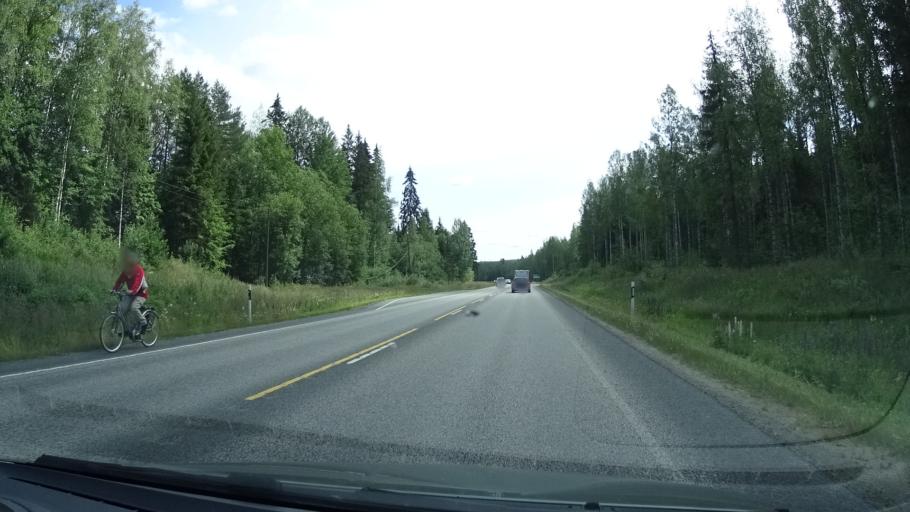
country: FI
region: Central Finland
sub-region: Jyvaeskylae
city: Jyvaeskylae
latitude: 62.2630
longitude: 25.5883
